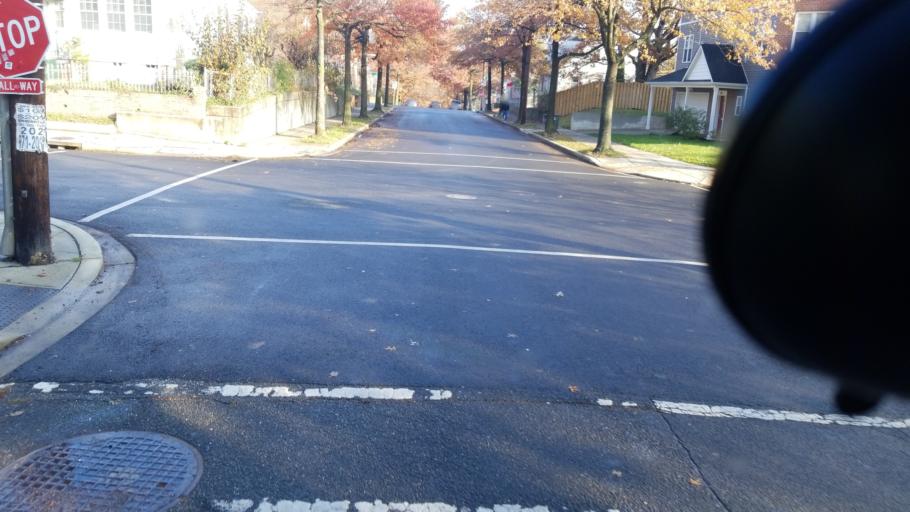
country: US
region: Maryland
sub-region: Prince George's County
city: Capitol Heights
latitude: 38.8853
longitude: -76.9260
